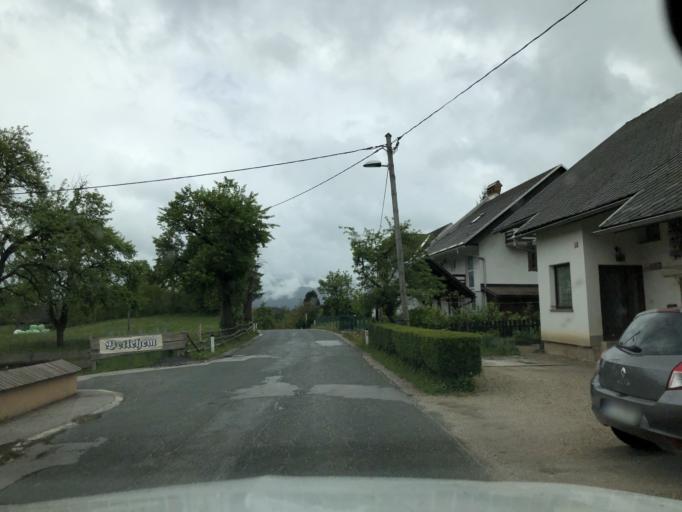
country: SI
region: Gorje
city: Zgornje Gorje
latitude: 46.3944
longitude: 14.0732
